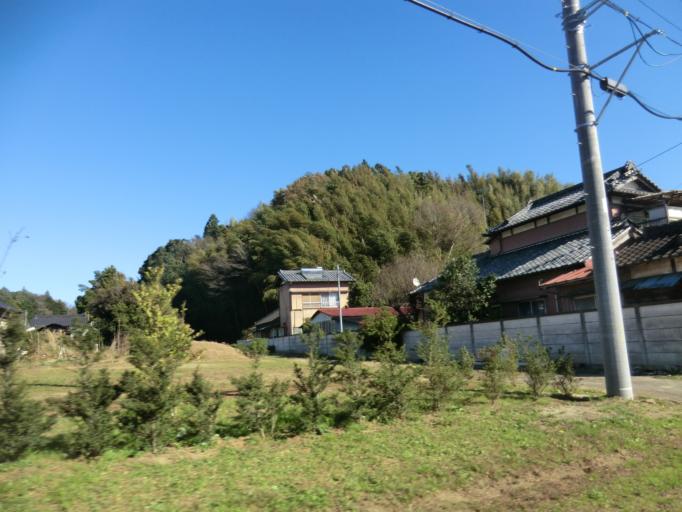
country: JP
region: Ibaraki
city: Ishioka
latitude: 36.1599
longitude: 140.3205
